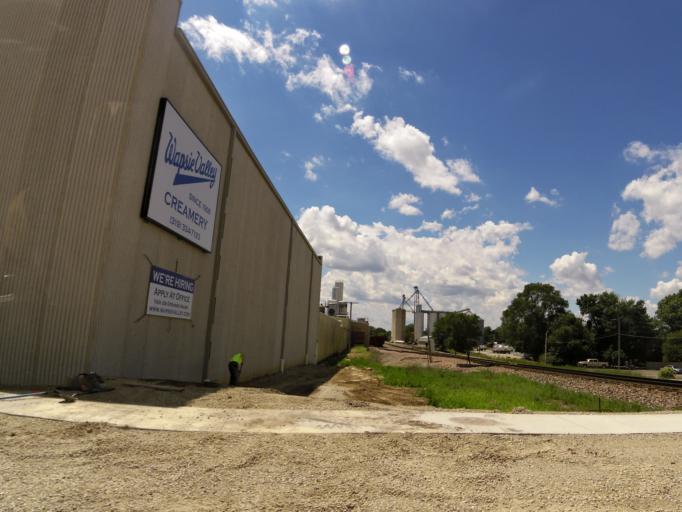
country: US
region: Iowa
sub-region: Buchanan County
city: Independence
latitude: 42.4779
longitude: -91.8894
